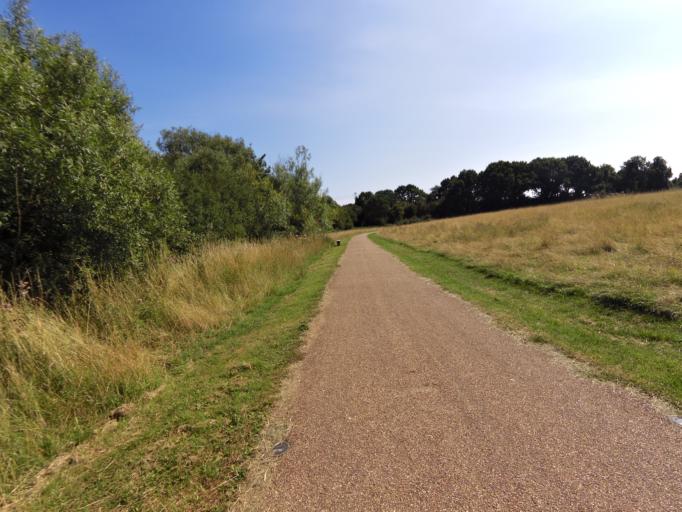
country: GB
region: England
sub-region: Essex
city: Colchester
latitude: 51.9009
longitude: 0.9157
